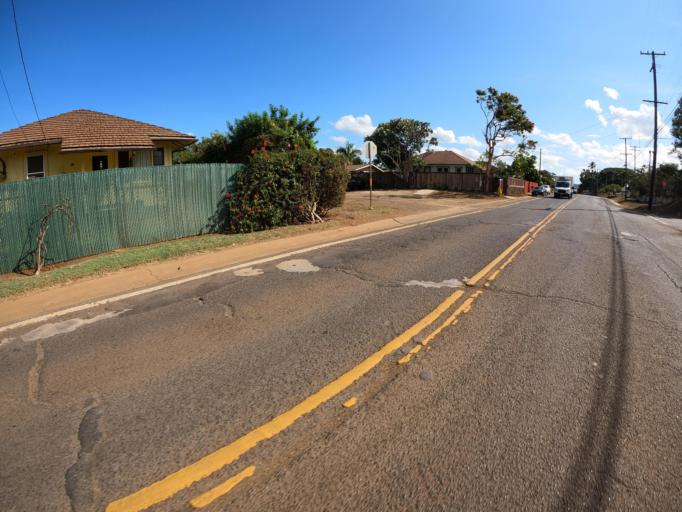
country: US
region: Hawaii
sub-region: Honolulu County
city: Waialua
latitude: 21.5677
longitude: -158.1282
